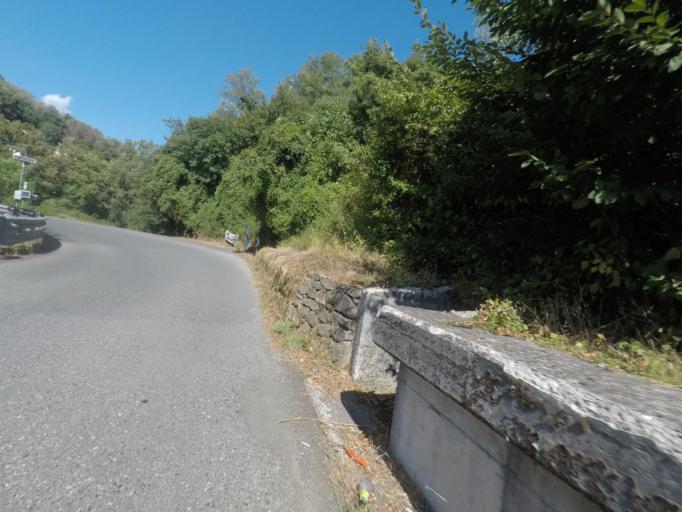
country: IT
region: Tuscany
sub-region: Provincia di Massa-Carrara
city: Pallerone
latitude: 44.2020
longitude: 10.0623
